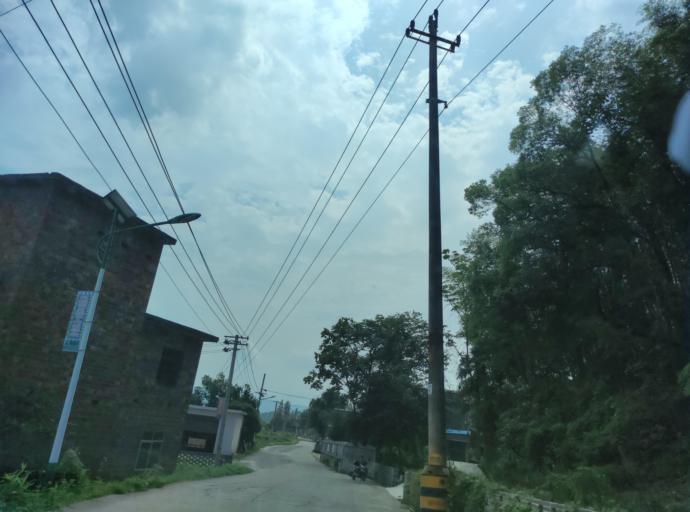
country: CN
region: Jiangxi Sheng
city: Yuannan
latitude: 27.6697
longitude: 114.0395
